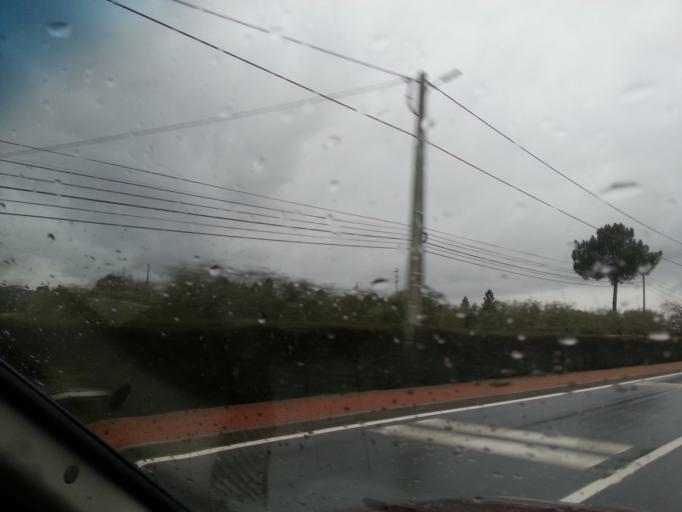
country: PT
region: Guarda
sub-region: Celorico da Beira
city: Celorico da Beira
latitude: 40.6402
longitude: -7.3726
